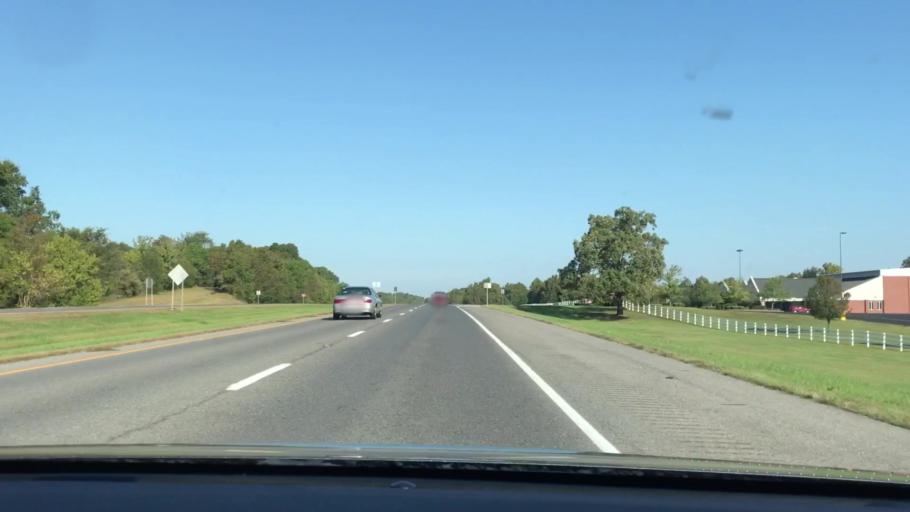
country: US
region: Kentucky
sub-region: Marshall County
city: Benton
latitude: 36.7681
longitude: -88.3129
